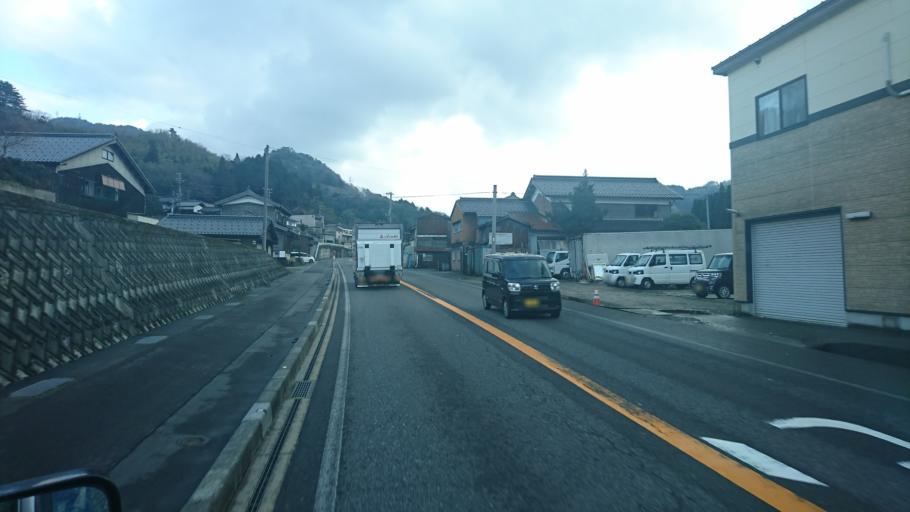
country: JP
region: Tottori
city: Tottori
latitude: 35.5487
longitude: 134.4975
